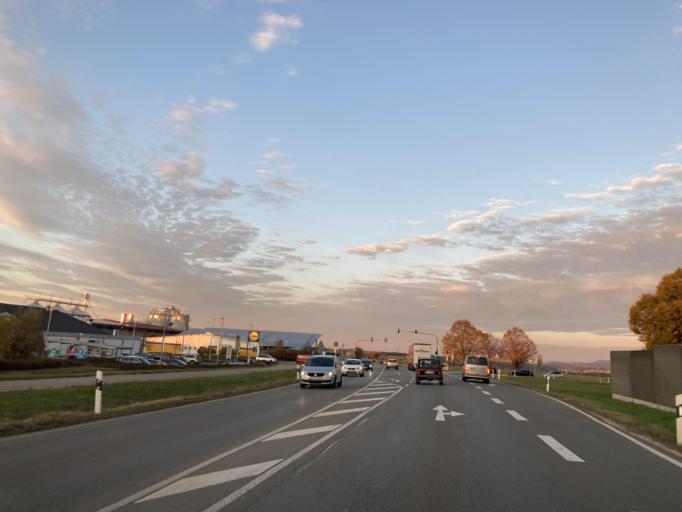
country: DE
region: Baden-Wuerttemberg
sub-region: Tuebingen Region
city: Dotternhausen
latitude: 48.2328
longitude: 8.7949
